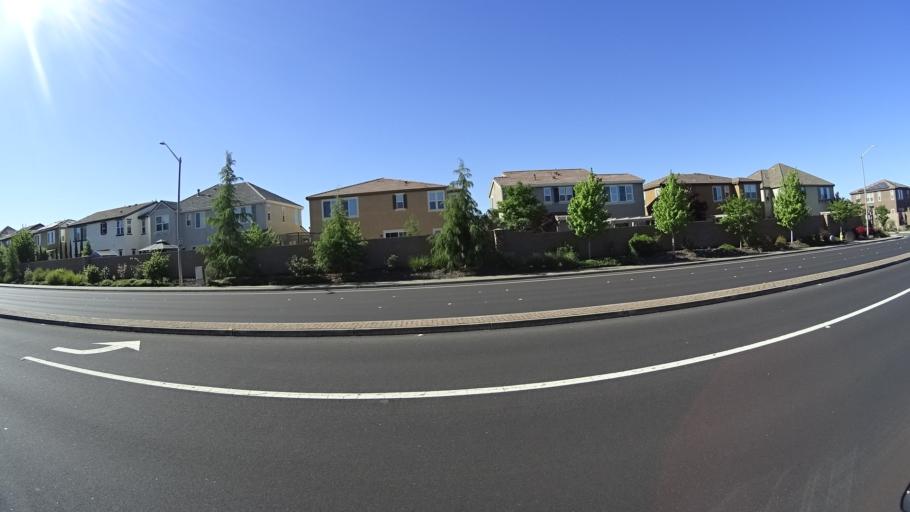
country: US
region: California
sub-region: Placer County
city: Rocklin
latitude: 38.8190
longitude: -121.2767
